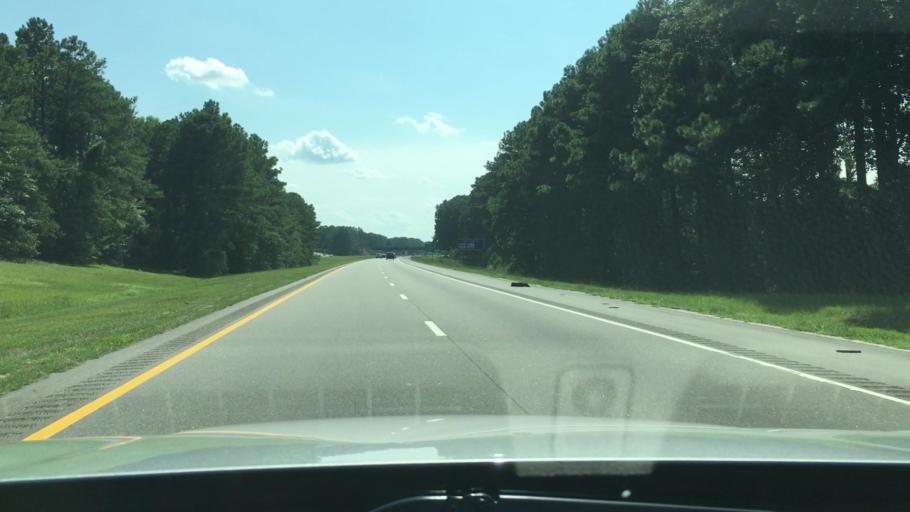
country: US
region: North Carolina
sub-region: Cumberland County
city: Hope Mills
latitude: 34.9422
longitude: -78.9145
